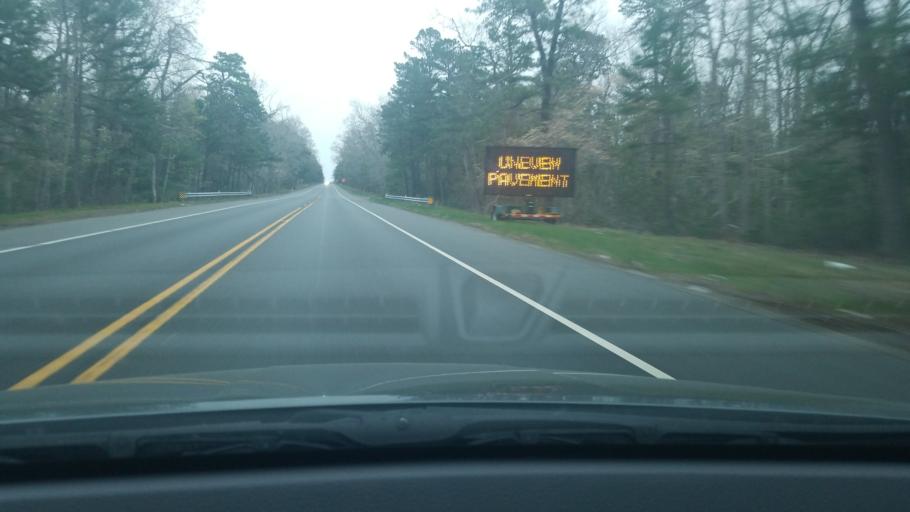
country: US
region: New Jersey
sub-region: Burlington County
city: Presidential Lakes Estates
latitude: 39.9013
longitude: -74.5886
